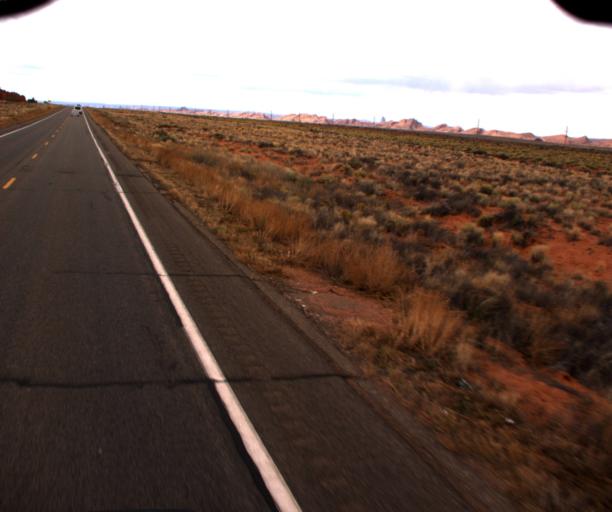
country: US
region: Arizona
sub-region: Navajo County
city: Kayenta
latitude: 36.7796
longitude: -109.9965
